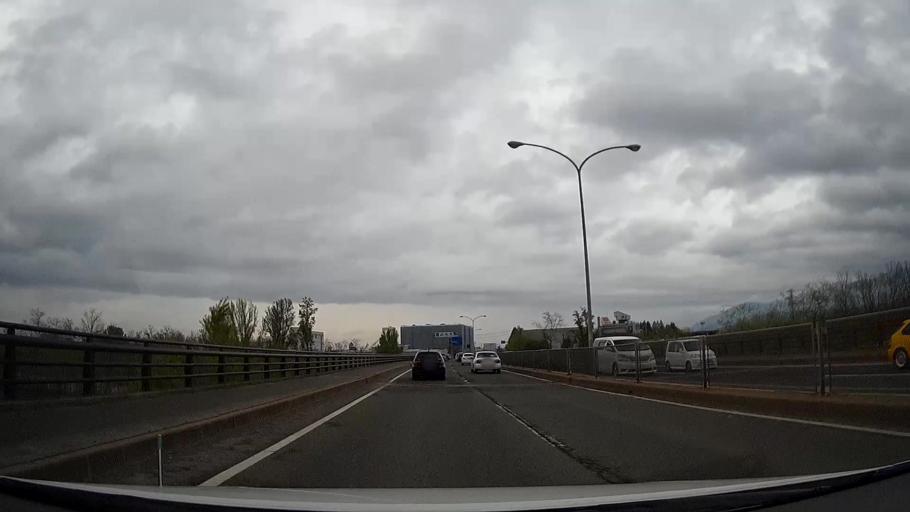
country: JP
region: Yamagata
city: Tendo
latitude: 38.3183
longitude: 140.3624
